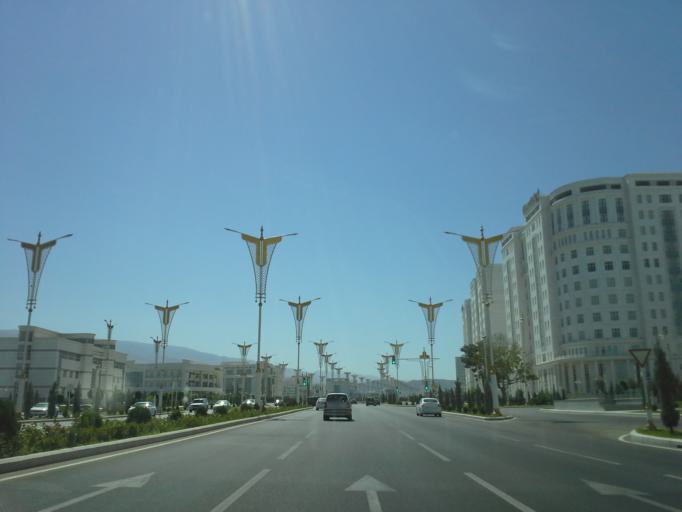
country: TM
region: Ahal
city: Ashgabat
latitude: 37.9141
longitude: 58.3559
